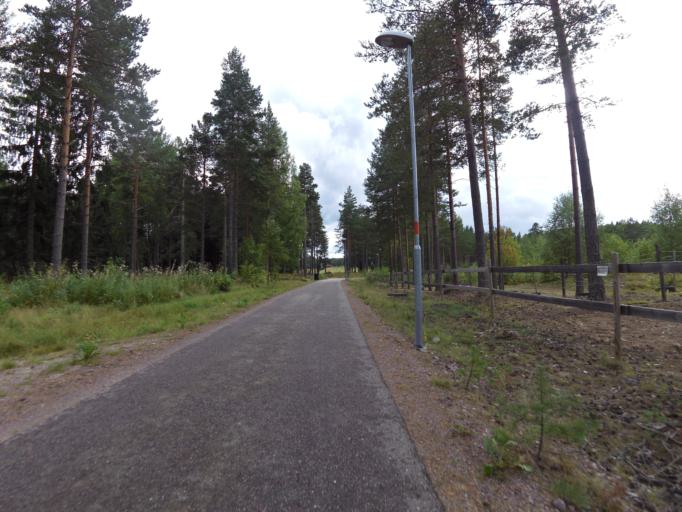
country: SE
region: Gaevleborg
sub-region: Sandvikens Kommun
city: Sandviken
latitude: 60.6785
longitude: 16.8163
